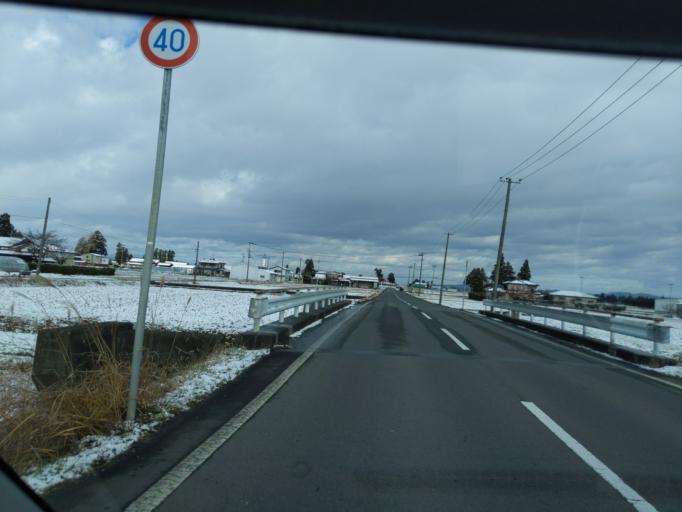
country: JP
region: Iwate
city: Mizusawa
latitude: 39.1522
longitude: 141.1134
